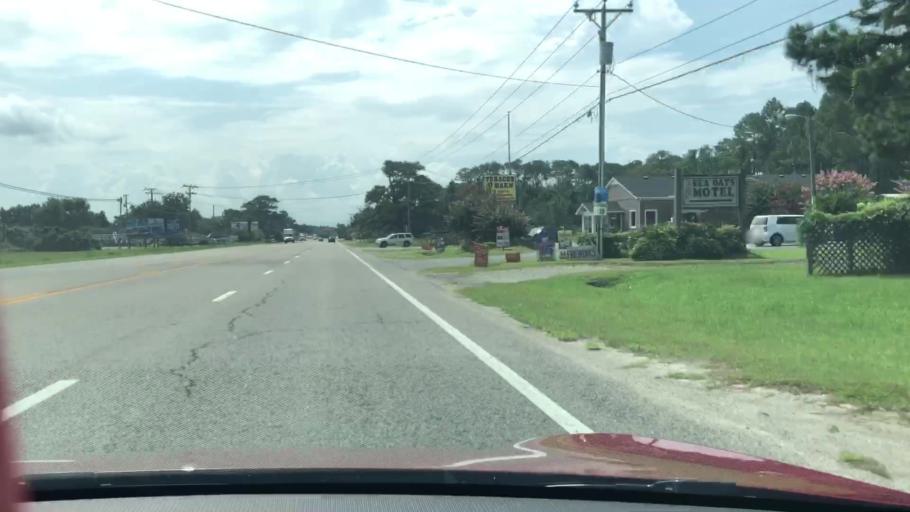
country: US
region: North Carolina
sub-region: Dare County
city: Southern Shores
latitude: 36.1710
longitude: -75.8610
